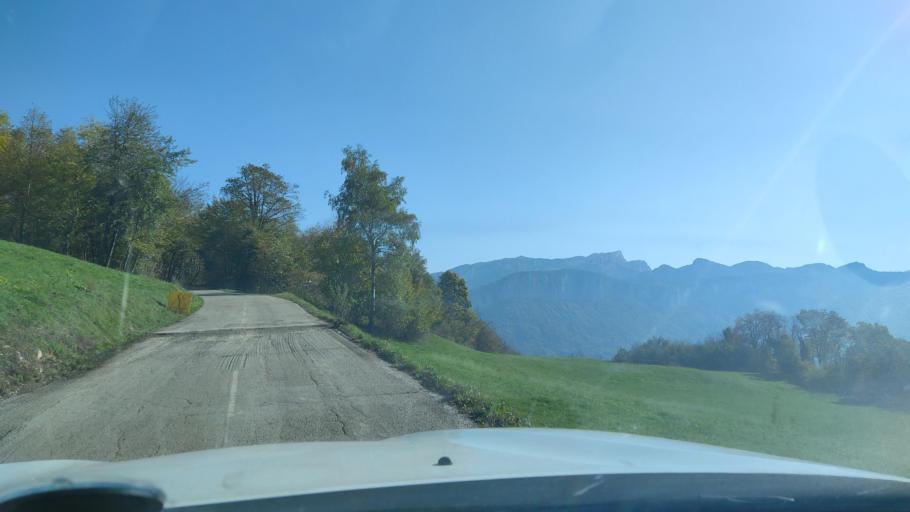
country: FR
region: Rhone-Alpes
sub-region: Departement de la Savoie
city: Les Echelles
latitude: 45.4626
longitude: 5.7672
